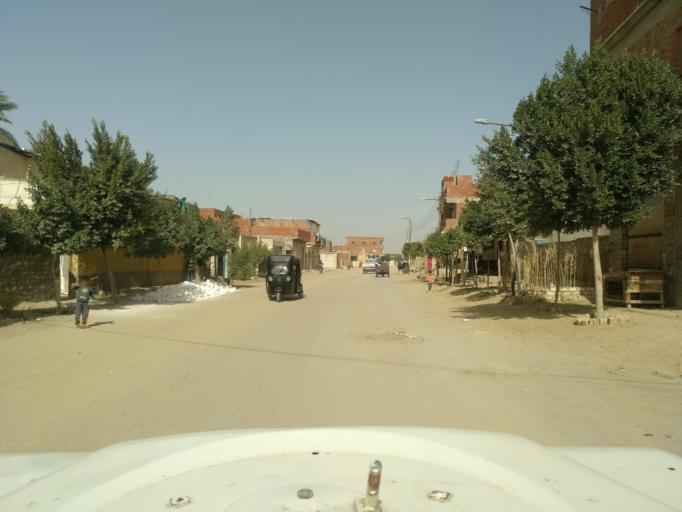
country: EG
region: Al Buhayrah
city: Beheira
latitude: 30.3822
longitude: 30.3432
